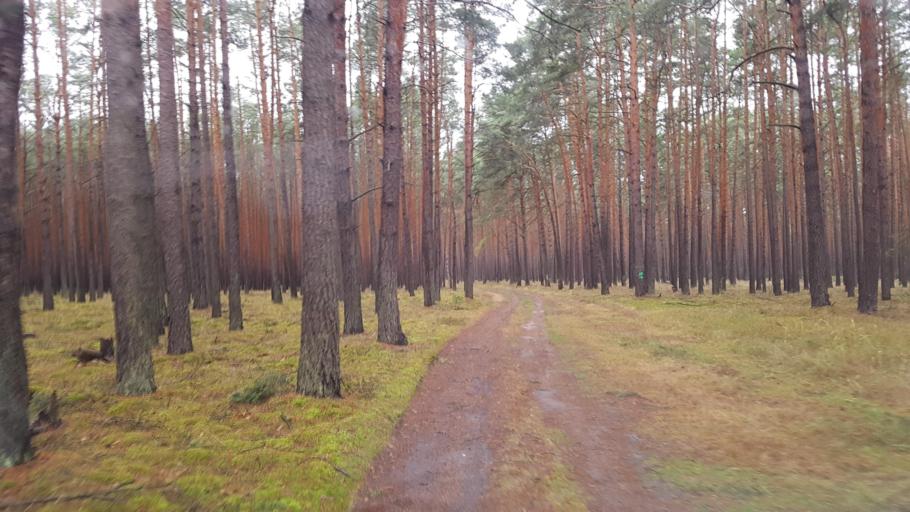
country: DE
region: Brandenburg
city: Tauche
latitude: 52.0951
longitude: 14.1108
